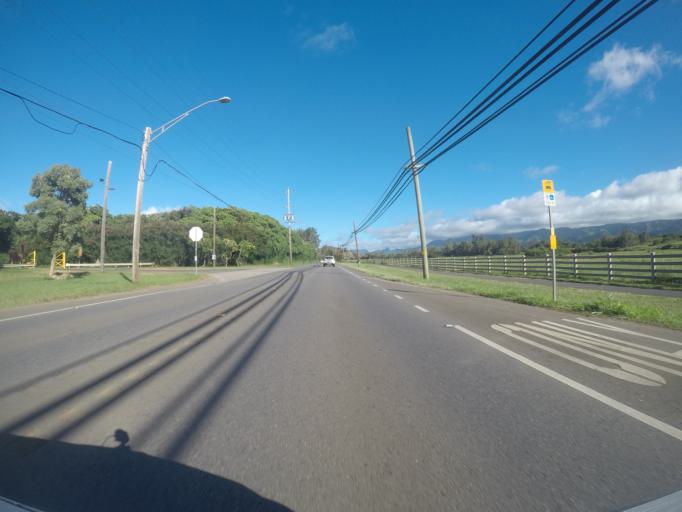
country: US
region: Hawaii
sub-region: Honolulu County
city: La'ie
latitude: 21.6603
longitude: -157.9334
